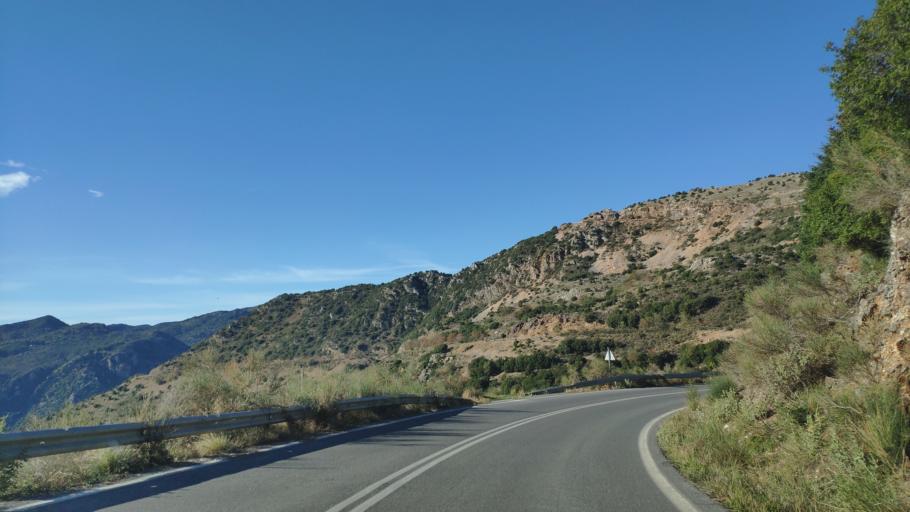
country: GR
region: Peloponnese
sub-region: Nomos Arkadias
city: Dimitsana
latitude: 37.5766
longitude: 22.0602
